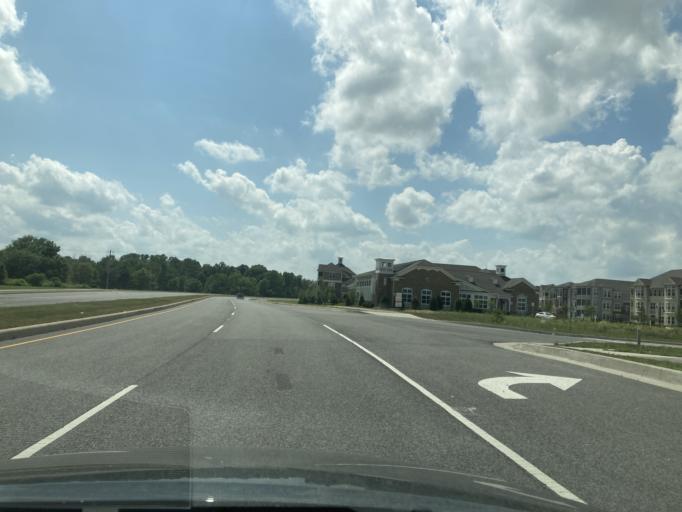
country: US
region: Indiana
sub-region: Hamilton County
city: Carmel
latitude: 40.0001
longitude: -86.1854
